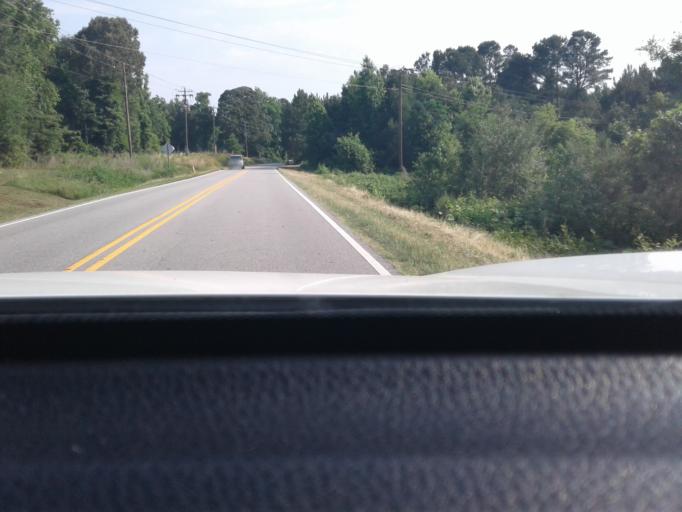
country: US
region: North Carolina
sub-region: Johnston County
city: Benson
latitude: 35.3969
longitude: -78.5430
